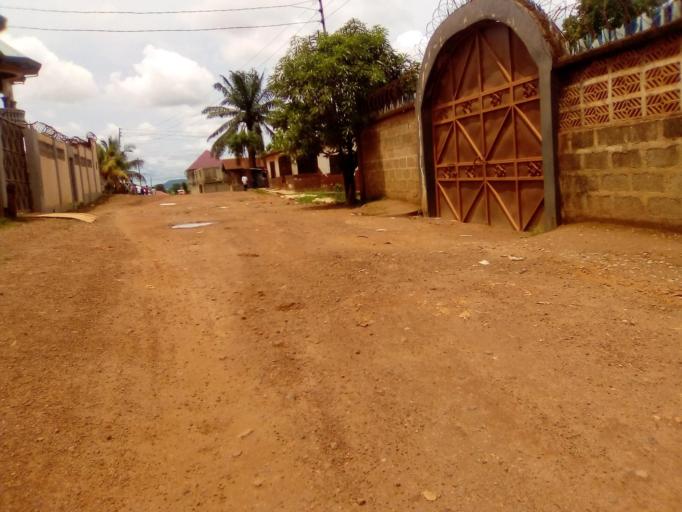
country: SL
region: Southern Province
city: Bo
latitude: 7.9328
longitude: -11.7205
